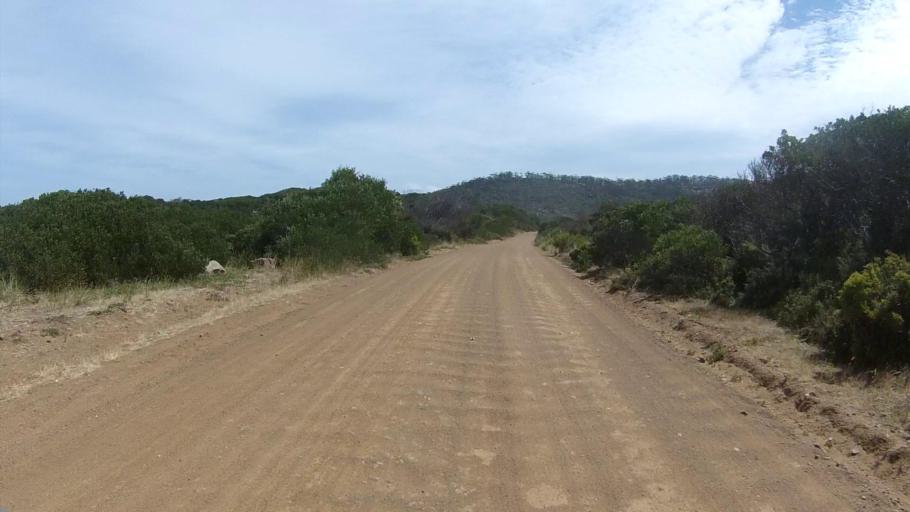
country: AU
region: Tasmania
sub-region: Clarence
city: Sandford
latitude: -43.0212
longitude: 147.4983
